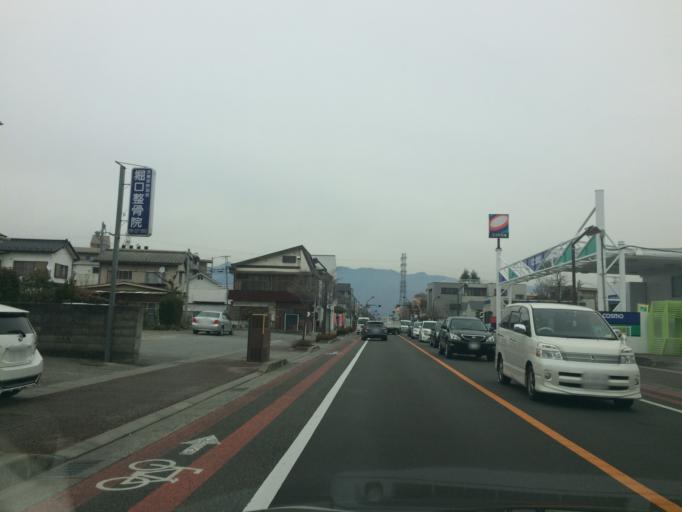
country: JP
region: Yamanashi
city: Kofu-shi
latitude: 35.6401
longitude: 138.5552
